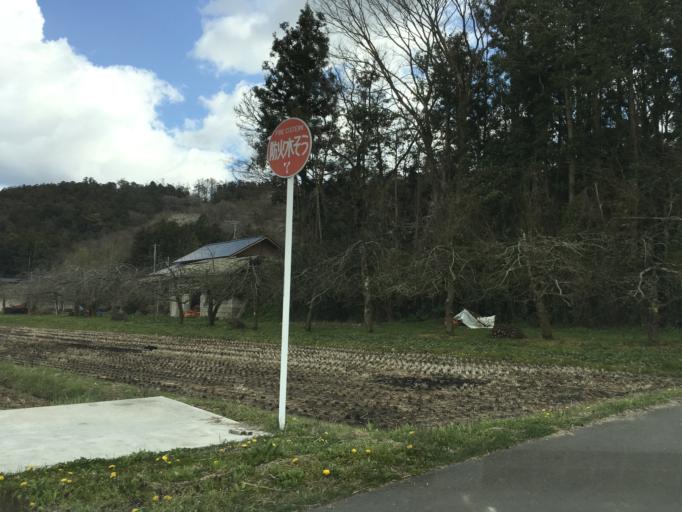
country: JP
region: Iwate
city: Ichinoseki
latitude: 38.7542
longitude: 141.2704
